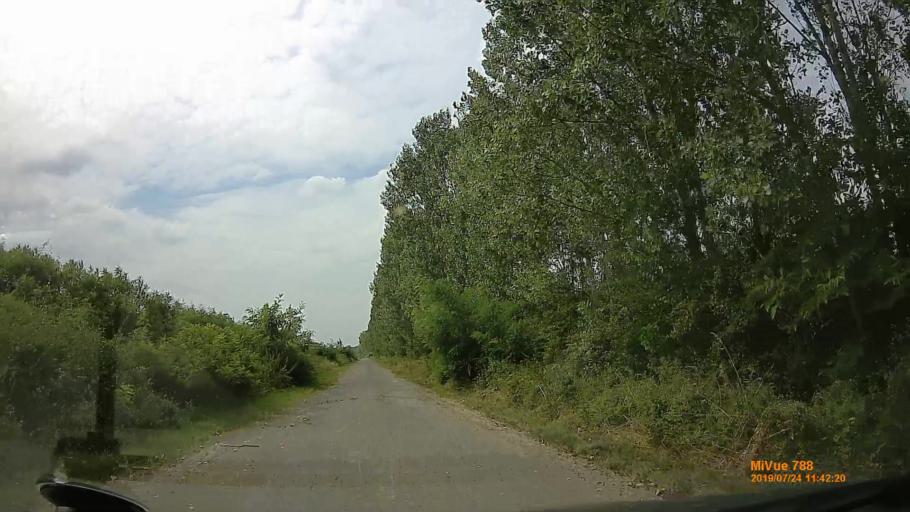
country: UA
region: Zakarpattia
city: Batiovo
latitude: 48.2368
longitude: 22.4596
